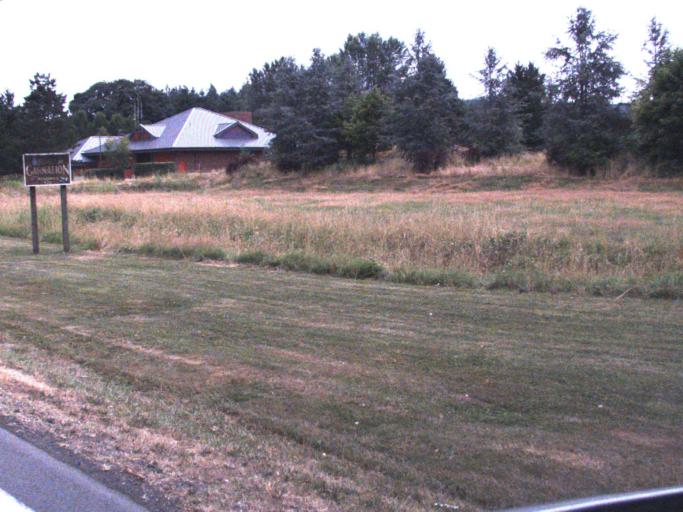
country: US
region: Washington
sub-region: King County
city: Carnation
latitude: 47.6400
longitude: -121.9163
